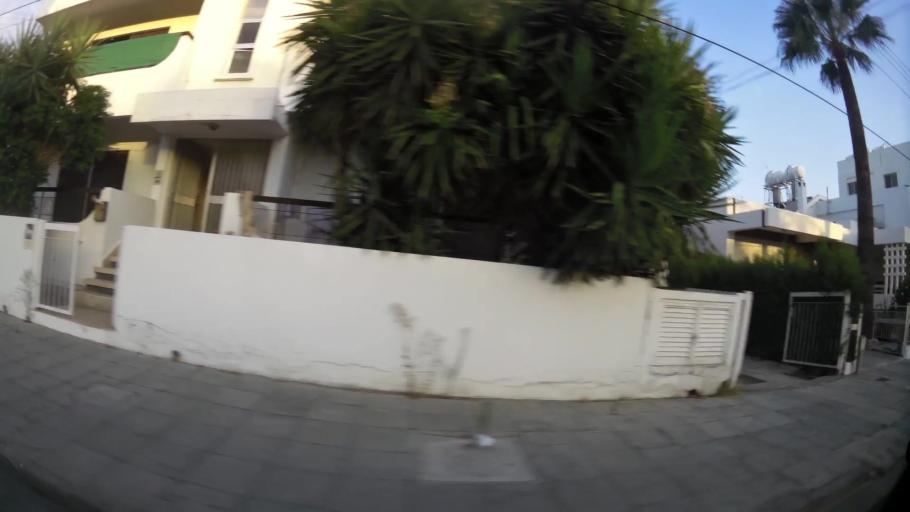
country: CY
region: Lefkosia
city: Nicosia
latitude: 35.1622
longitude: 33.3133
